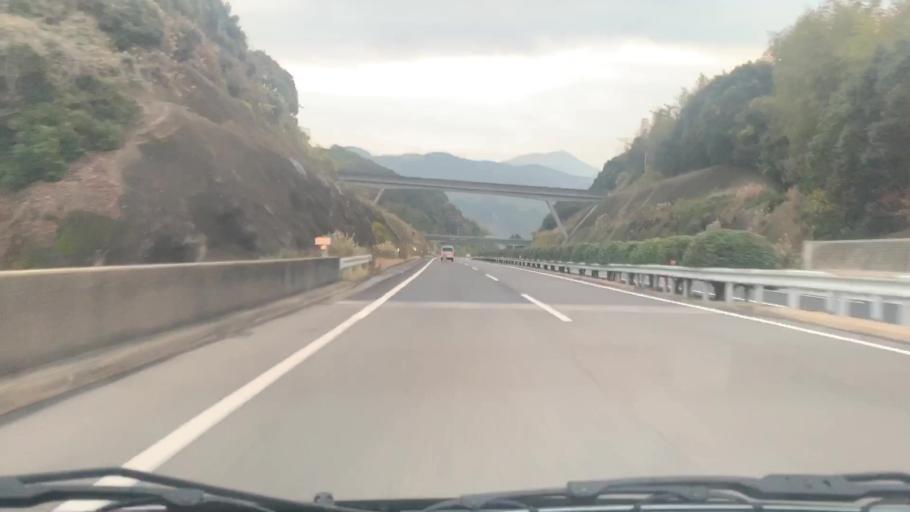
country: JP
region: Nagasaki
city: Omura
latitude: 33.0278
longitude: 129.9344
